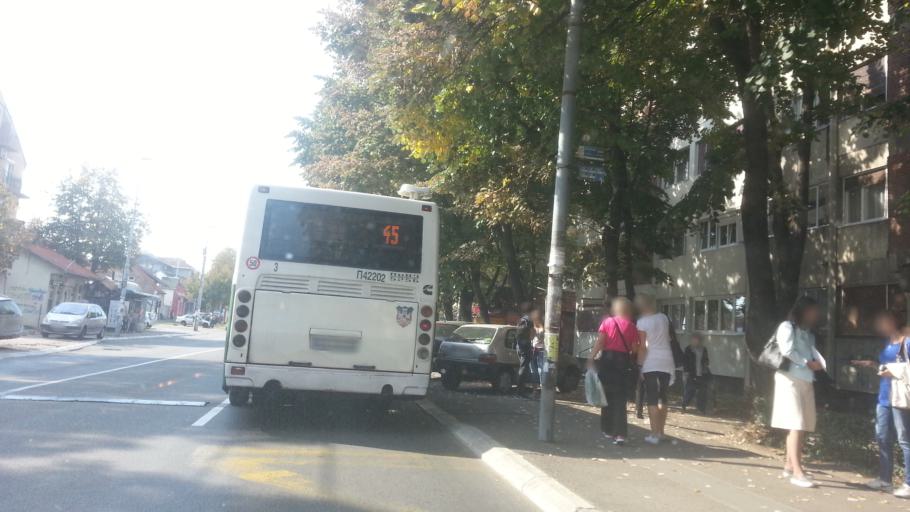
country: RS
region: Central Serbia
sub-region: Belgrade
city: Zemun
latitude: 44.8499
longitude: 20.3876
